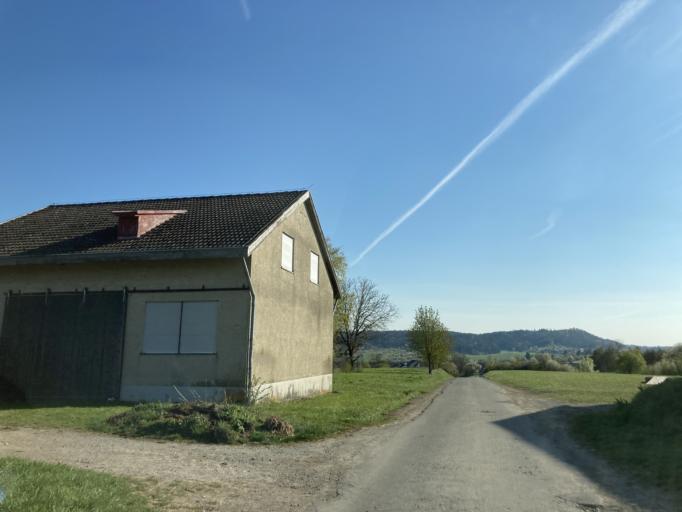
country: DE
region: Baden-Wuerttemberg
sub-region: Tuebingen Region
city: Rottenburg
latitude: 48.5405
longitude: 8.9521
